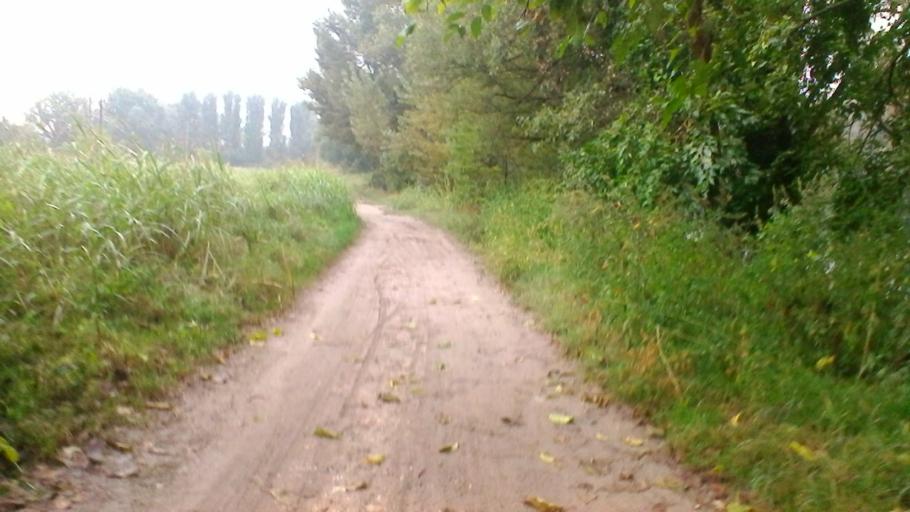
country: IT
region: Veneto
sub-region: Provincia di Verona
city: Montorio
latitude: 45.4272
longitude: 11.0415
